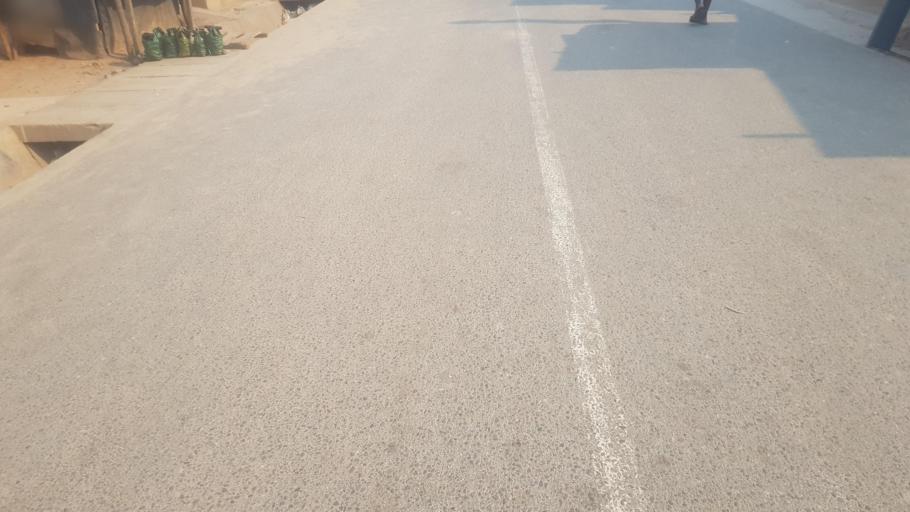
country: ZM
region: Lusaka
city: Lusaka
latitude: -15.4422
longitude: 28.3846
